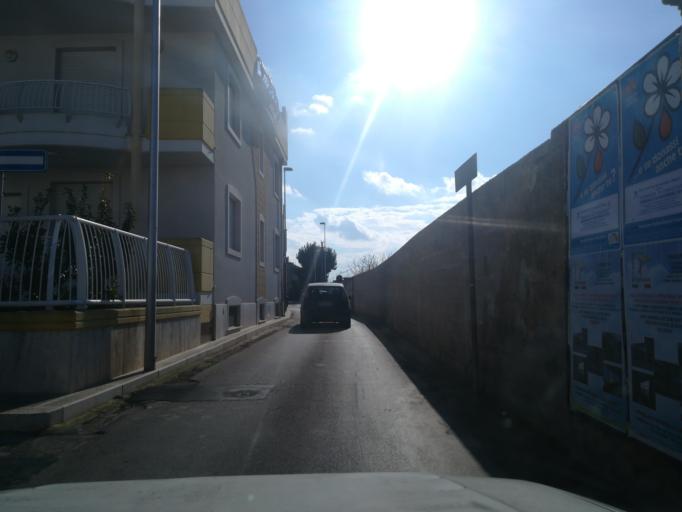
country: IT
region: Apulia
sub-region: Provincia di Bari
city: Modugno
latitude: 41.0786
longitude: 16.7765
